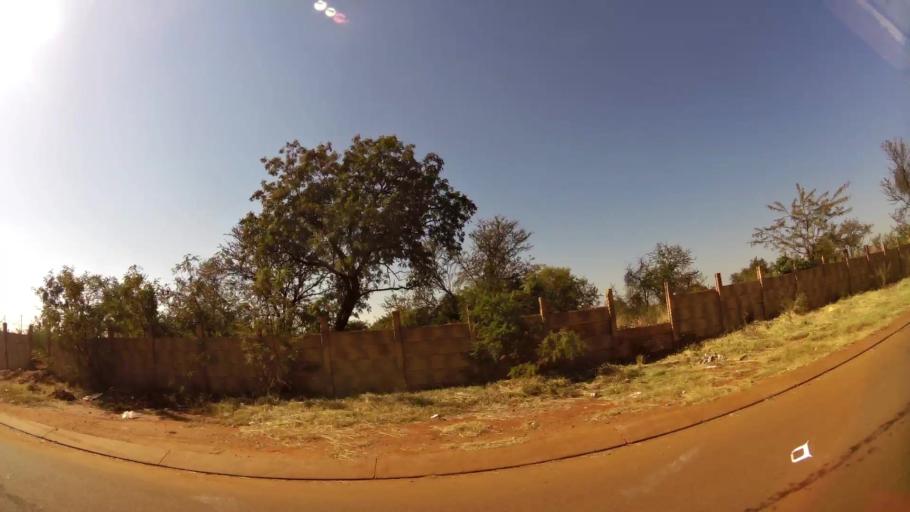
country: ZA
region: North-West
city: Ga-Rankuwa
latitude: -25.6361
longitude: 28.0844
